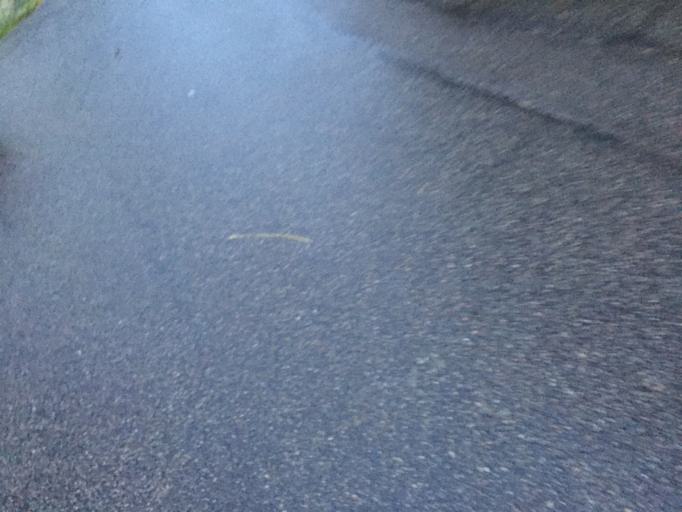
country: SE
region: Vaestra Goetaland
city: Ronnang
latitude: 57.9235
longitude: 11.5850
